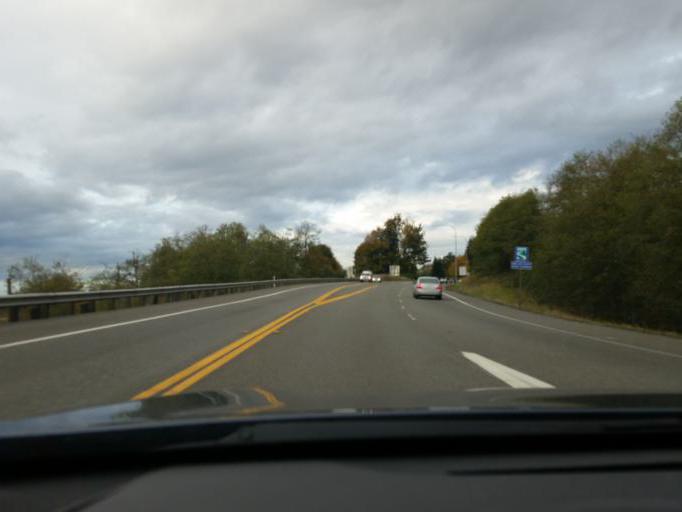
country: US
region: Washington
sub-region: Snohomish County
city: Fobes Hill
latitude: 47.9811
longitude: -122.1377
